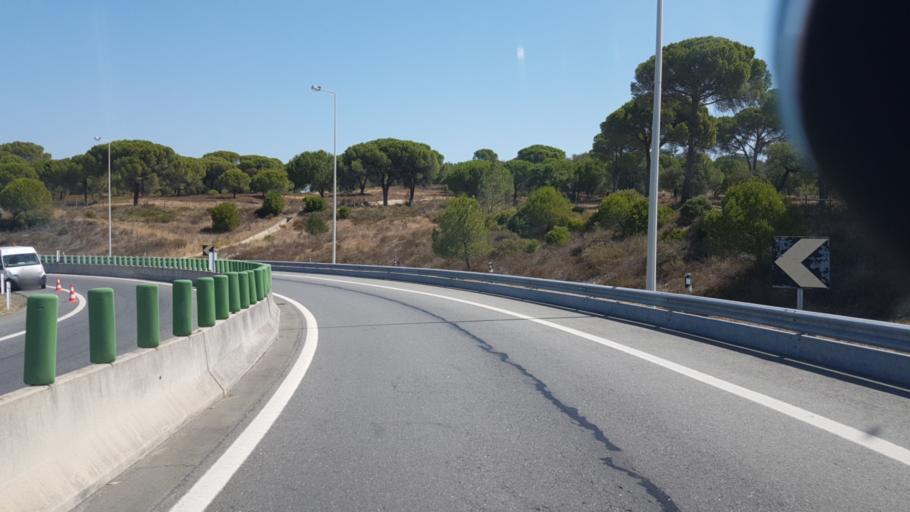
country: PT
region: Setubal
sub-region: Alcacer do Sal
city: Alcacer do Sal
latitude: 38.4184
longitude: -8.5111
